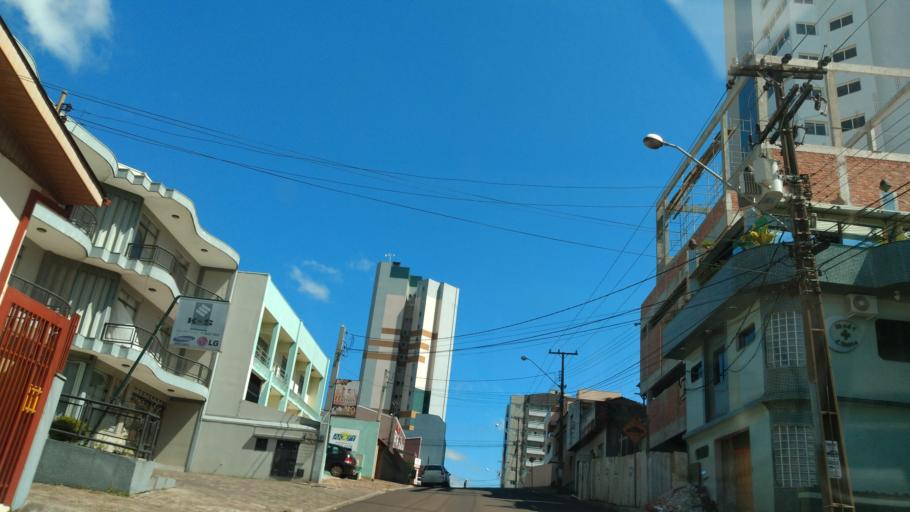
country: BR
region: Parana
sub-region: Guarapuava
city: Guarapuava
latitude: -25.3977
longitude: -51.4684
